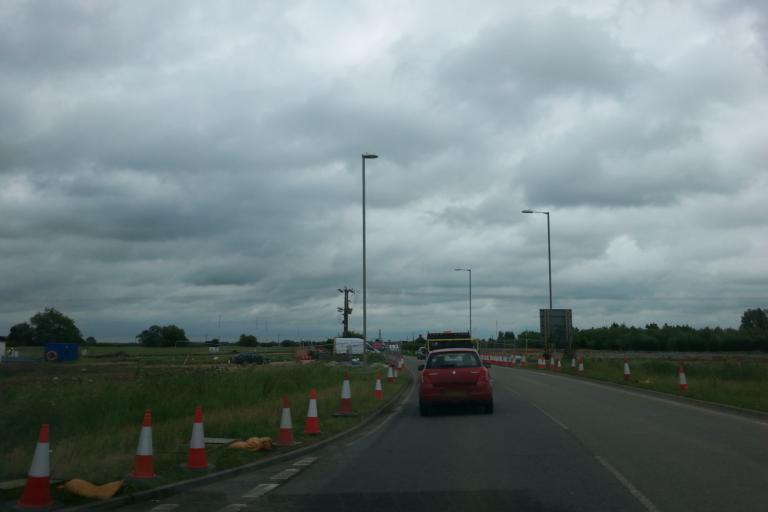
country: GB
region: England
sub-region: Cambridgeshire
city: Swavesey
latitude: 52.2590
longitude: 0.0255
